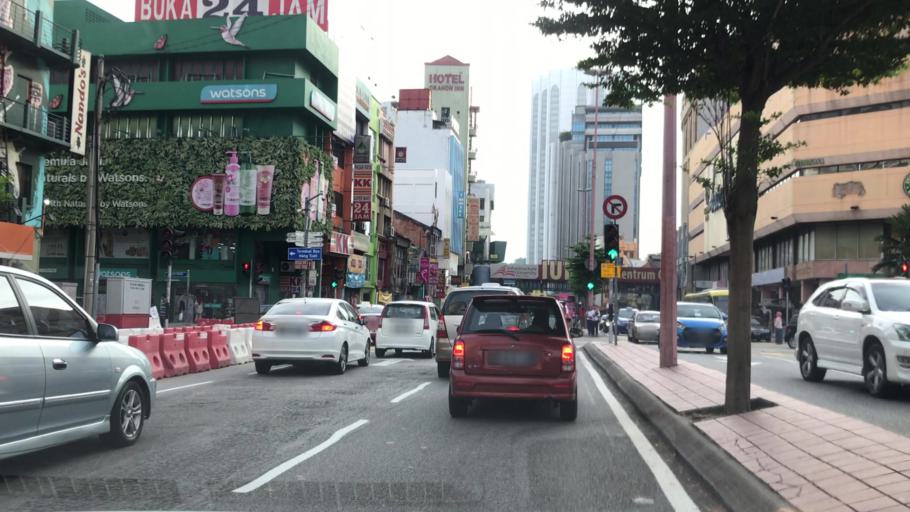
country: MY
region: Kuala Lumpur
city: Kuala Lumpur
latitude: 3.1455
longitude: 101.6989
